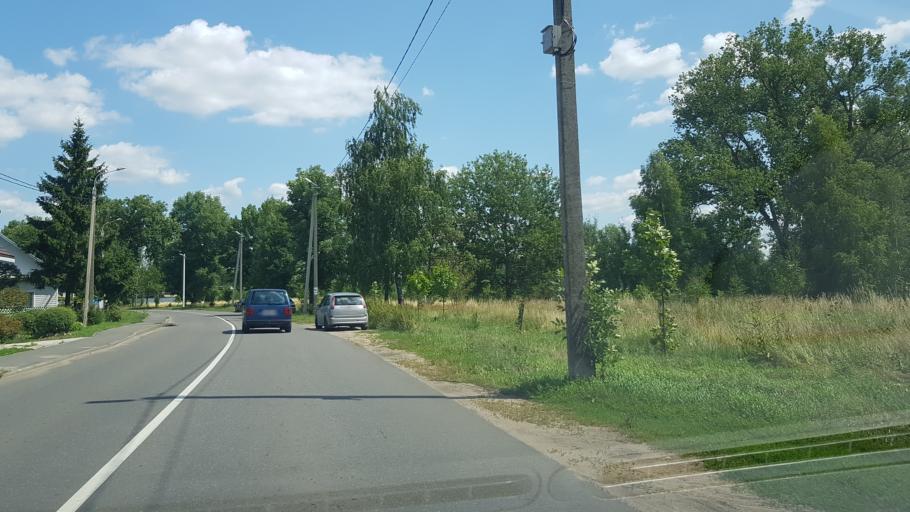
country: BY
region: Mogilev
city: Babruysk
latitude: 53.1150
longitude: 29.2186
